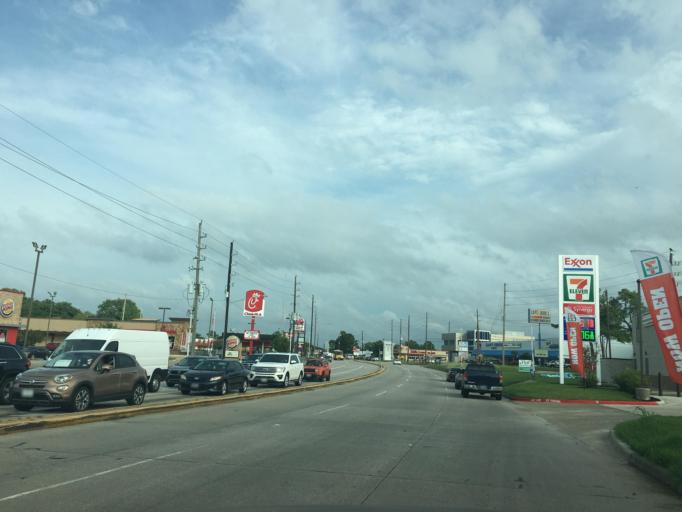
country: US
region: Texas
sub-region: Montgomery County
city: Oak Ridge North
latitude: 30.1273
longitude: -95.4547
